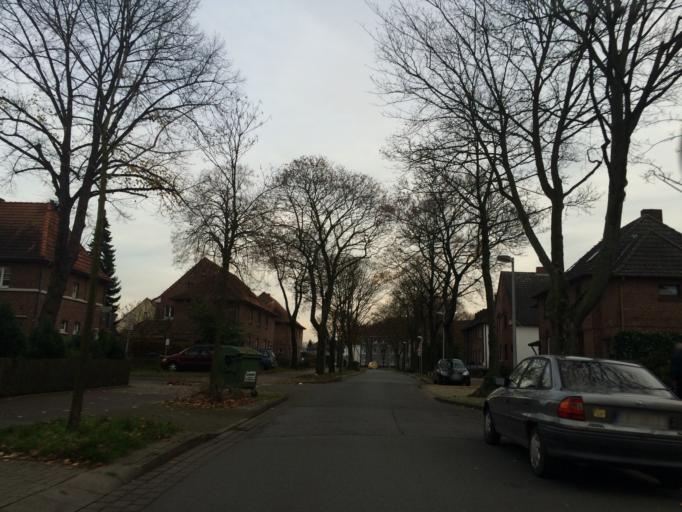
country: DE
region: North Rhine-Westphalia
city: Dorsten
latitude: 51.6681
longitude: 6.9823
